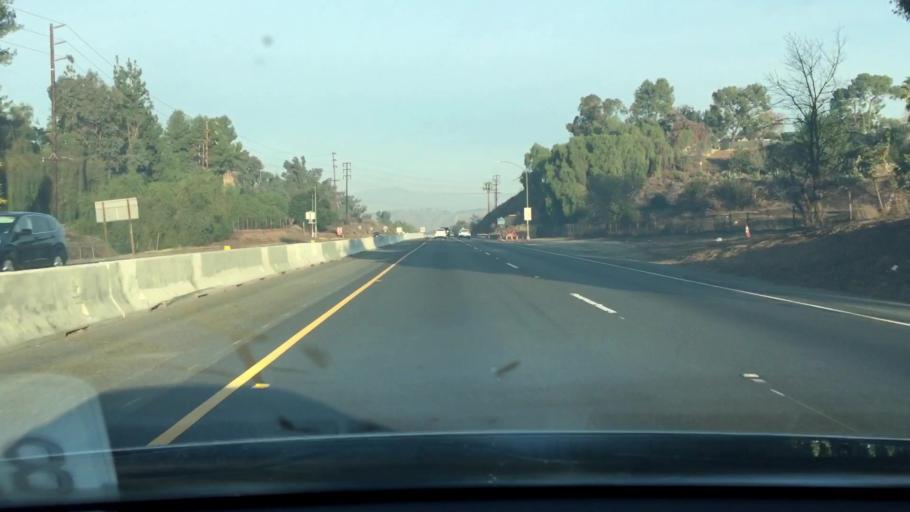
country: US
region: California
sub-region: Los Angeles County
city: Pomona
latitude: 34.0425
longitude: -117.7695
